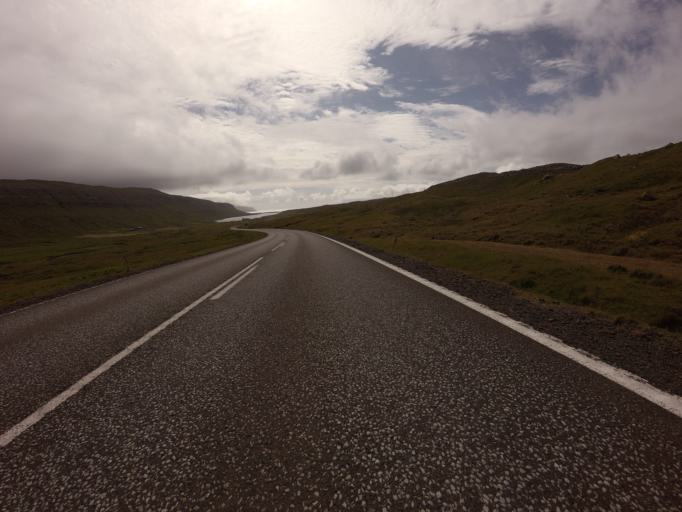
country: FO
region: Sandoy
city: Sandur
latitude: 61.8681
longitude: -6.8440
